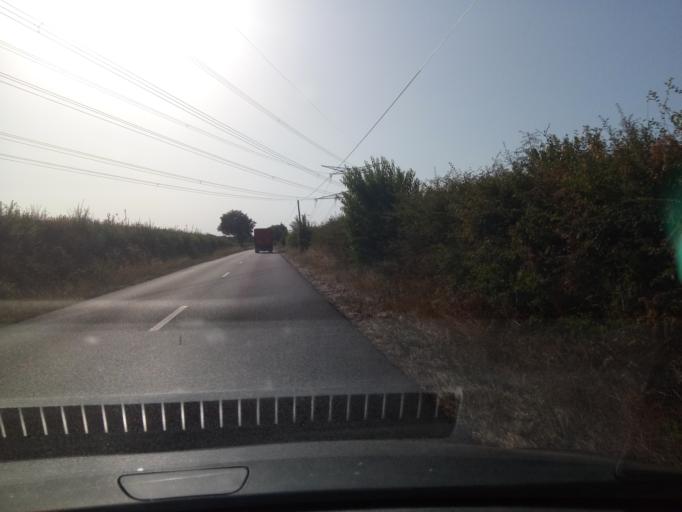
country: FR
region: Poitou-Charentes
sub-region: Departement de la Vienne
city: Montmorillon
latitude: 46.4460
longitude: 0.9768
